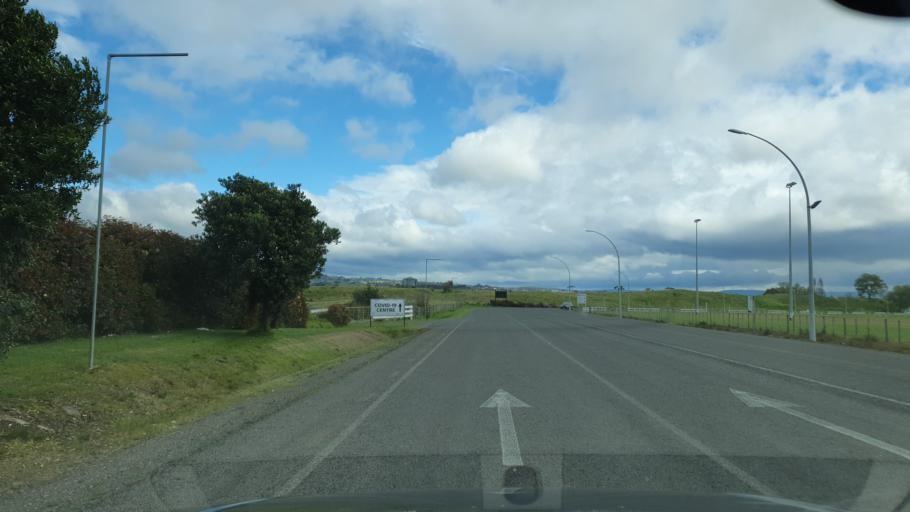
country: NZ
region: Bay of Plenty
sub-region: Tauranga City
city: Tauranga
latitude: -37.6863
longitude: 176.2287
